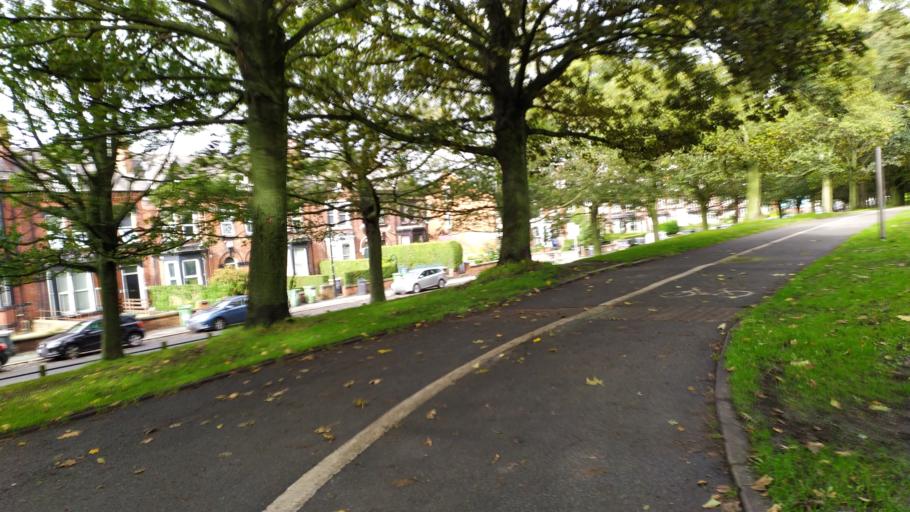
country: GB
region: England
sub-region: City and Borough of Leeds
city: Leeds
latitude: 53.8101
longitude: -1.5651
